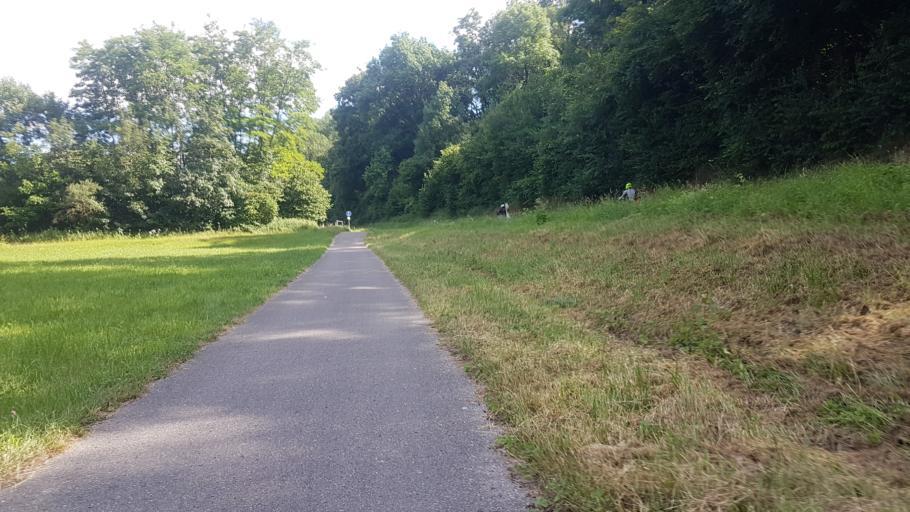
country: DE
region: Baden-Wuerttemberg
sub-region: Regierungsbezirk Stuttgart
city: Jagsthausen
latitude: 49.3262
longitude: 9.4834
